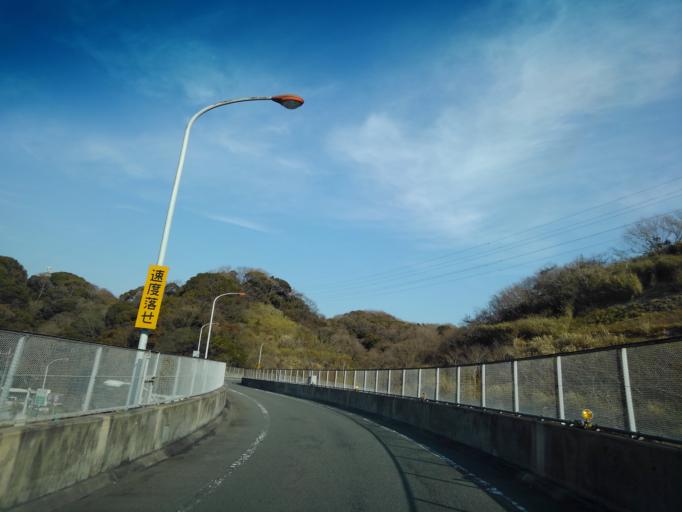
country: JP
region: Kanagawa
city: Yokosuka
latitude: 35.2750
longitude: 139.6386
